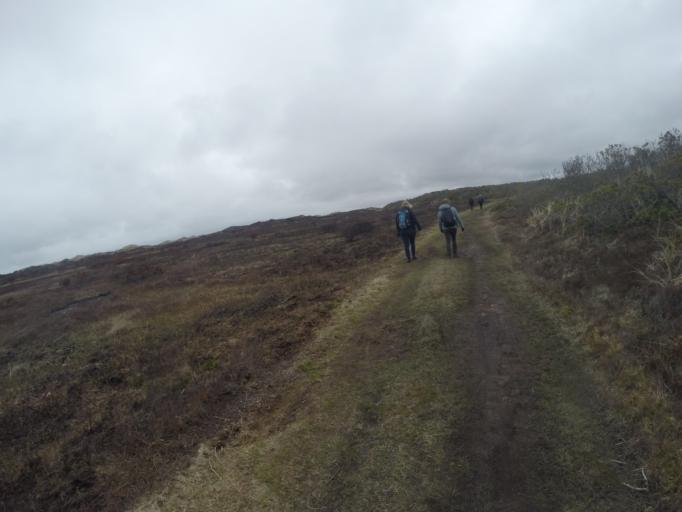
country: DK
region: Central Jutland
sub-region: Lemvig Kommune
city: Thyboron
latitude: 56.8485
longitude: 8.2827
